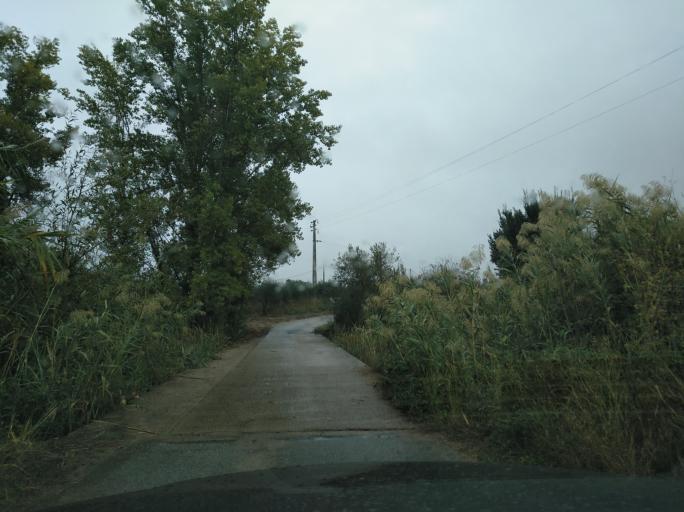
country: PT
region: Portalegre
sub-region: Campo Maior
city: Campo Maior
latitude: 38.9496
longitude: -7.0869
